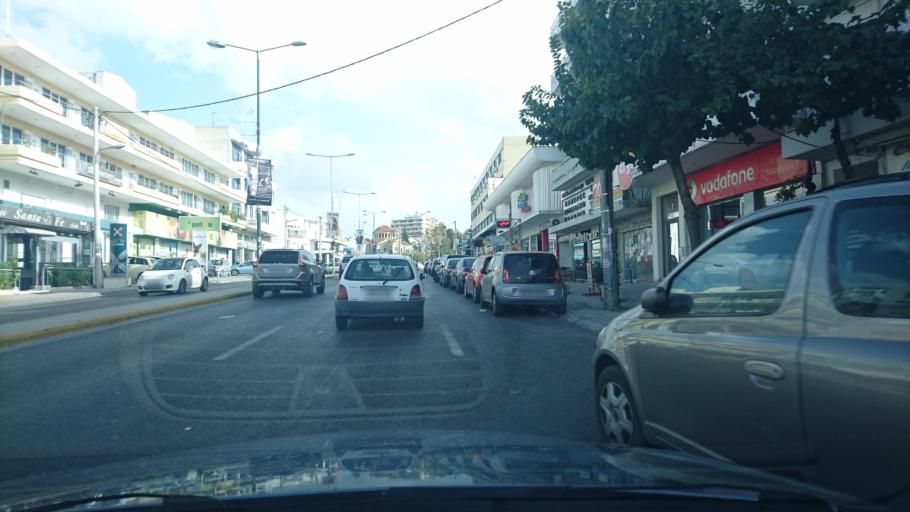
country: GR
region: Attica
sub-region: Nomarchia Athinas
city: Agia Paraskevi
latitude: 38.0141
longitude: 23.8189
